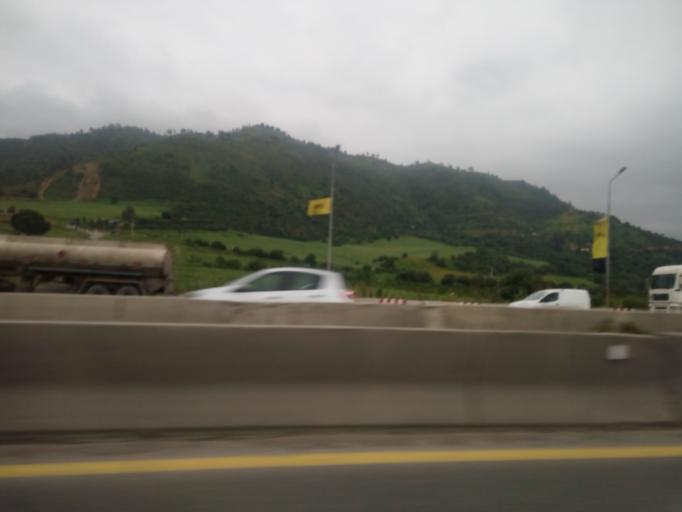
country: DZ
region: Bouira
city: Lakhdaria
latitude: 36.5539
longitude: 3.5900
